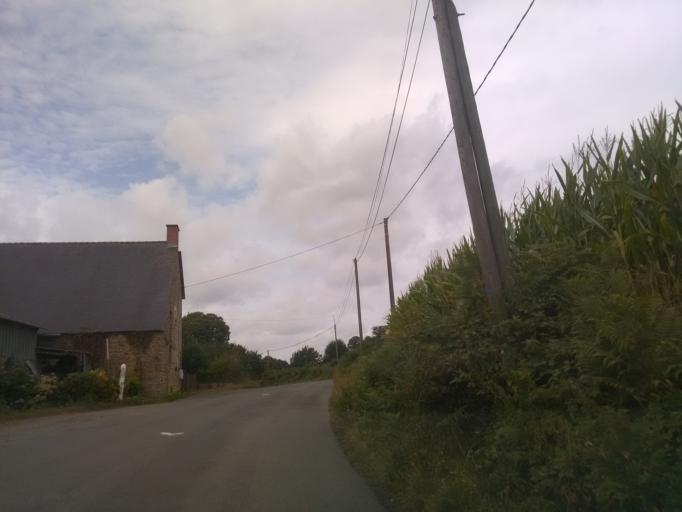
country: FR
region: Brittany
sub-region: Departement d'Ille-et-Vilaine
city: Dinge
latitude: 48.3547
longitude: -1.7440
